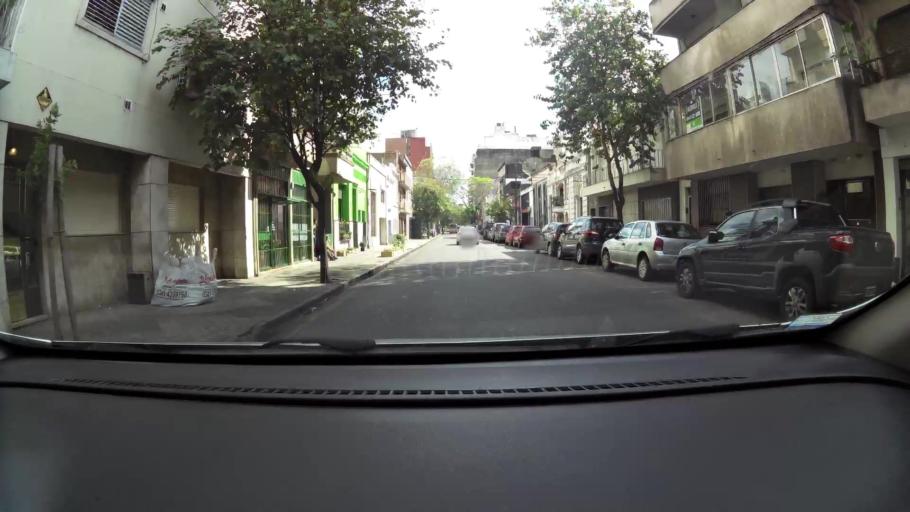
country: AR
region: Santa Fe
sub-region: Departamento de Rosario
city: Rosario
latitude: -32.9523
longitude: -60.6469
